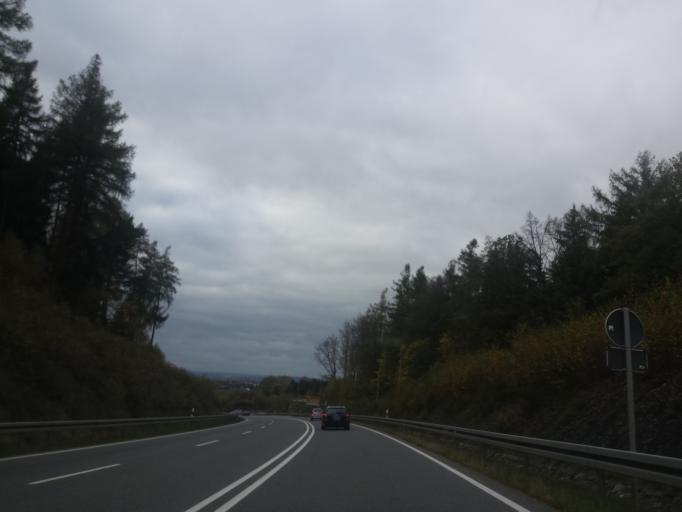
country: DE
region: Saxony
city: Stollberg
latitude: 50.6953
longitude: 12.7966
